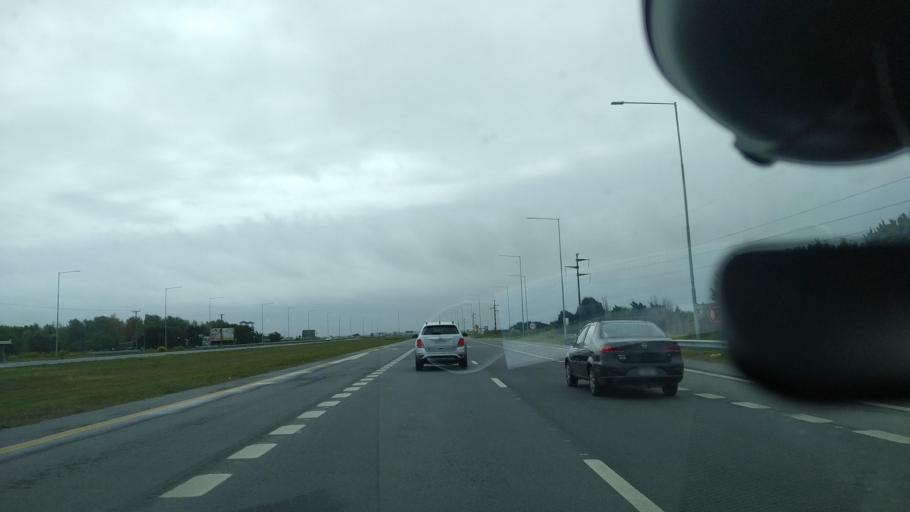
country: AR
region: Buenos Aires
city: San Clemente del Tuyu
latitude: -36.4431
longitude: -56.7138
